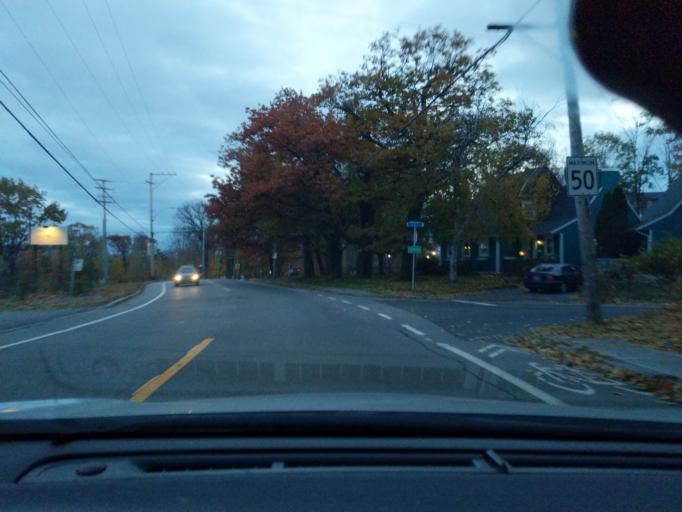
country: CA
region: Quebec
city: Quebec
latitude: 46.7763
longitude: -71.2533
